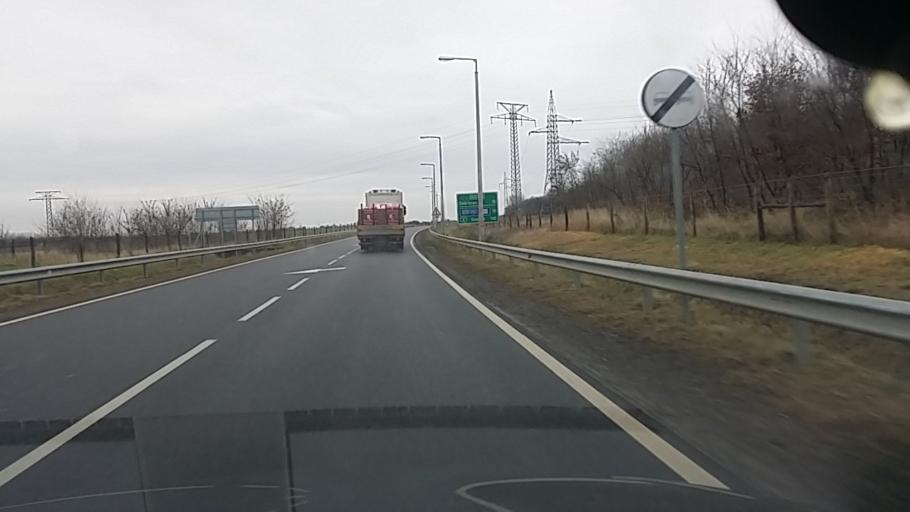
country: HU
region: Hajdu-Bihar
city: Hajduhadhaz
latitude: 47.6637
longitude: 21.6525
